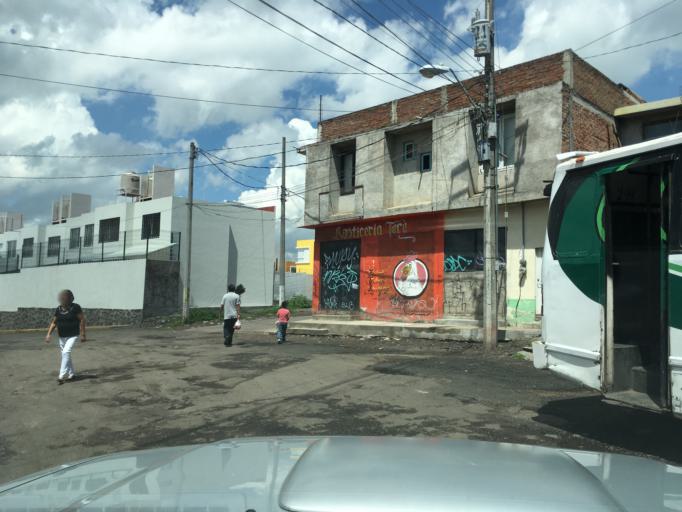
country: MX
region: Michoacan
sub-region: Tarimbaro
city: Real Hacienda (Metropolis)
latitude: 19.7299
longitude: -101.2068
